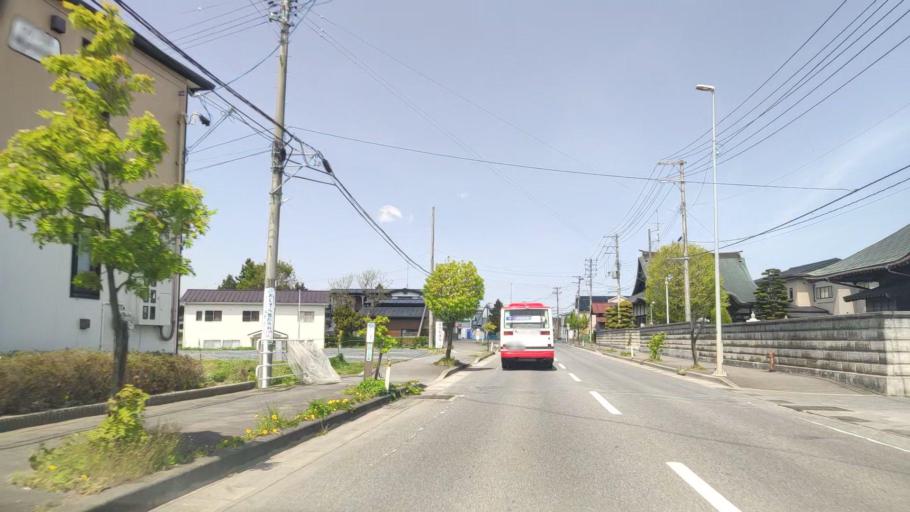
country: JP
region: Aomori
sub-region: Hachinohe Shi
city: Uchimaru
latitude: 40.5045
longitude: 141.4393
